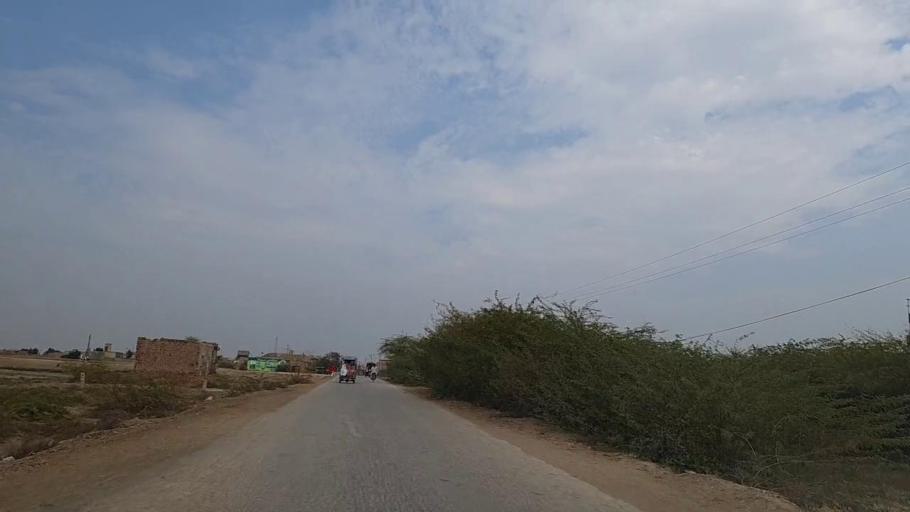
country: PK
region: Sindh
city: Naukot
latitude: 24.9578
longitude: 69.2866
